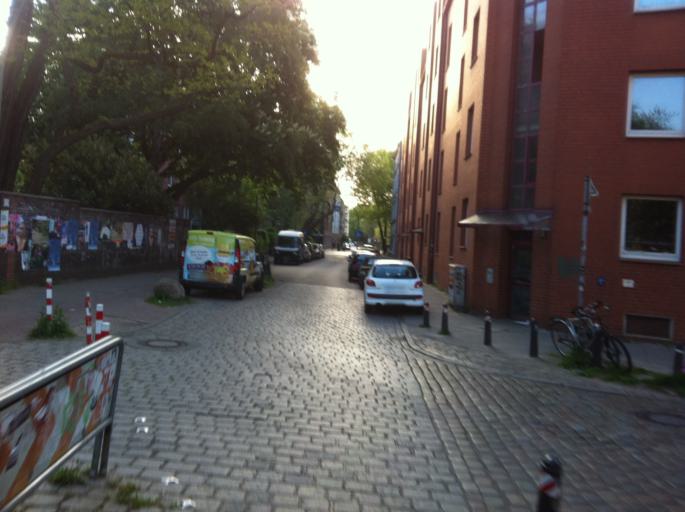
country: DE
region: Hamburg
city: Altona
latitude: 53.5557
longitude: 9.9469
